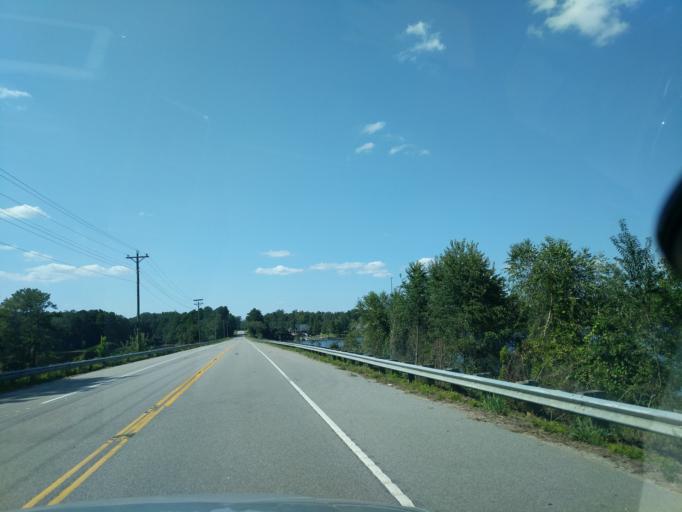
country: US
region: South Carolina
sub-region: Newberry County
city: Prosperity
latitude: 34.0820
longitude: -81.5636
